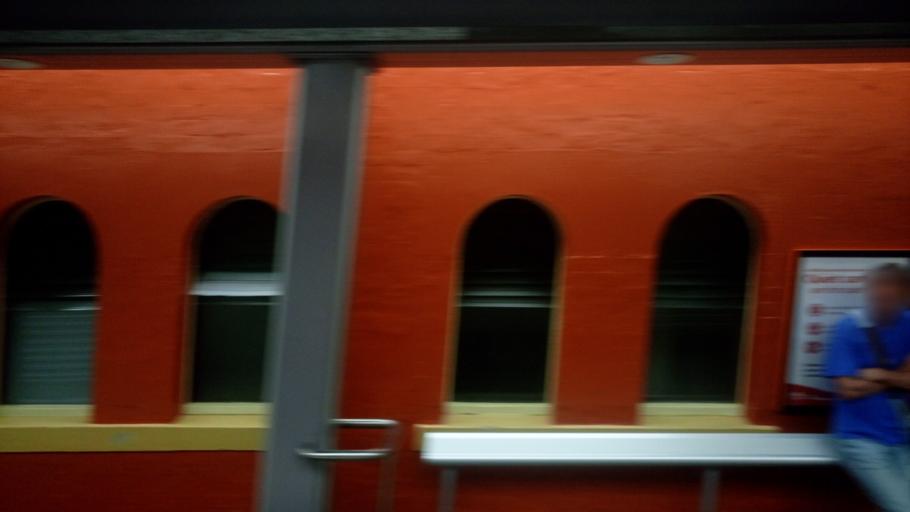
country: AU
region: New South Wales
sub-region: Parramatta
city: Paramatta
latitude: -33.8178
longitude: 151.0054
